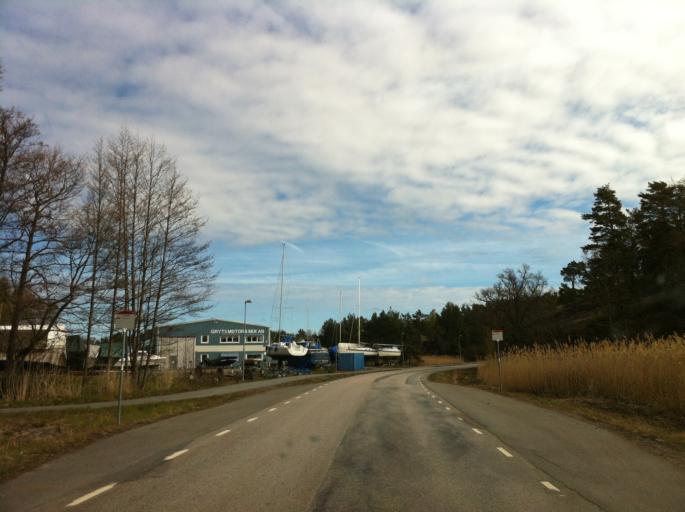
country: SE
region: OEstergoetland
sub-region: Valdemarsviks Kommun
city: Valdemarsvik
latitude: 58.1878
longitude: 16.8155
